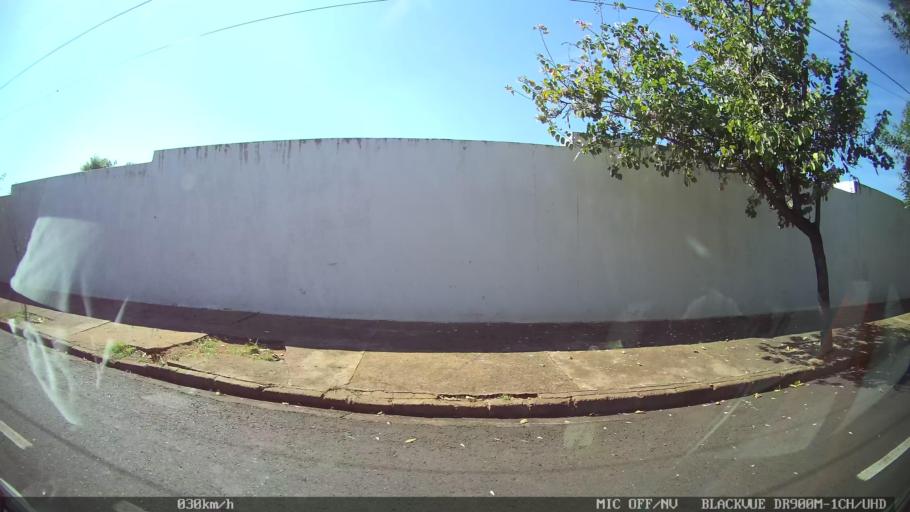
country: BR
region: Sao Paulo
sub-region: Sao Jose Do Rio Preto
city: Sao Jose do Rio Preto
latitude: -20.8152
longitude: -49.4106
